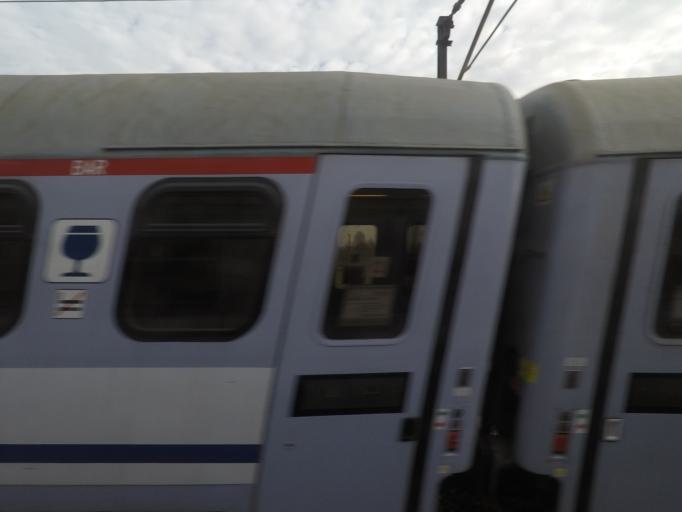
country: PL
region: Subcarpathian Voivodeship
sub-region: Powiat przemyski
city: Zurawica
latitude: 49.8254
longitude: 22.8327
